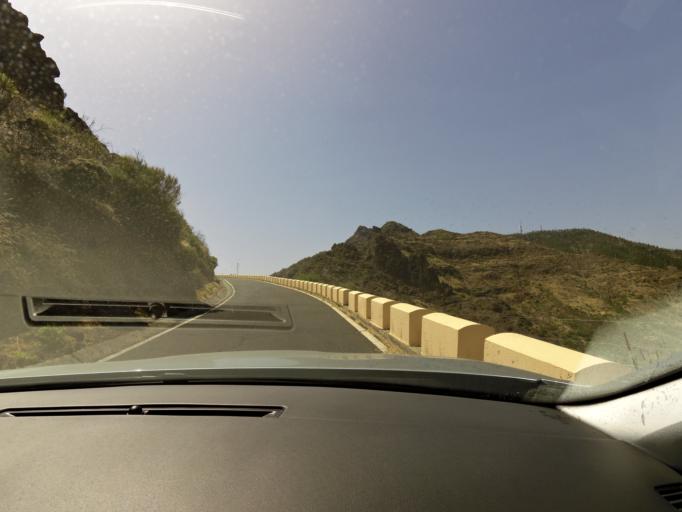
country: ES
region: Canary Islands
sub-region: Provincia de Santa Cruz de Tenerife
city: Santiago del Teide
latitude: 28.2985
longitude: -16.8219
